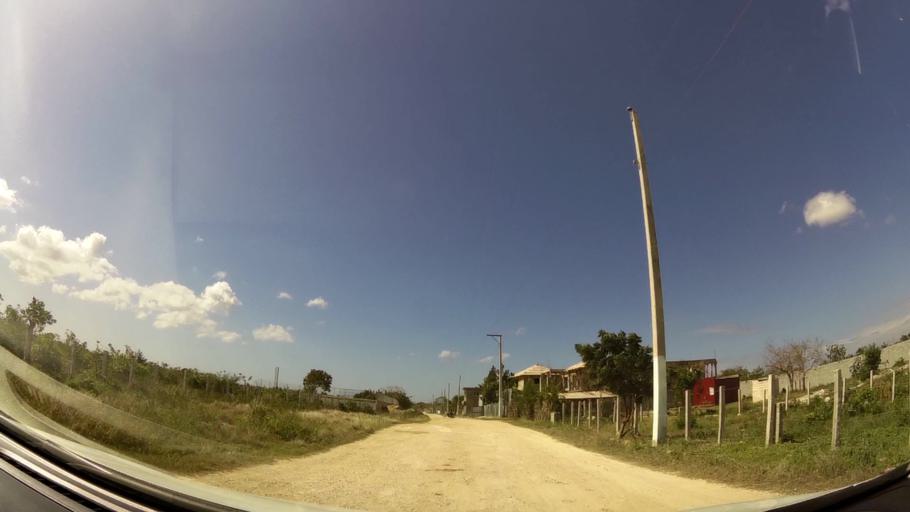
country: DO
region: Santo Domingo
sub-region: Santo Domingo
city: Boca Chica
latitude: 18.4638
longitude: -69.6225
